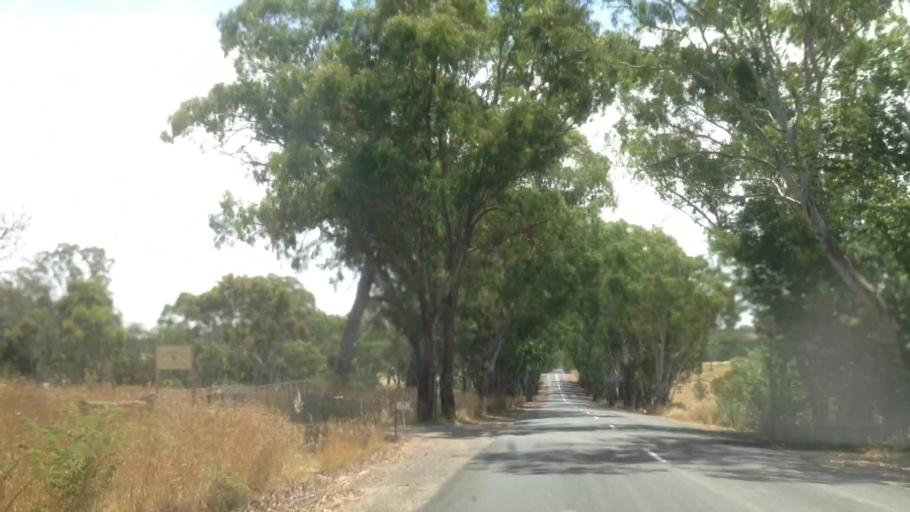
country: AU
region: South Australia
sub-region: Adelaide Hills
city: Birdwood
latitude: -34.7912
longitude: 138.9634
